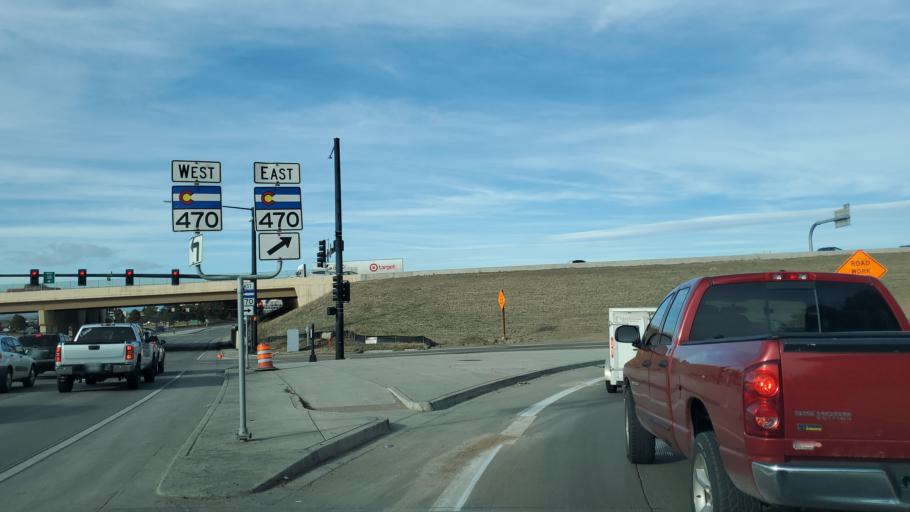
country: US
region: Colorado
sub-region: Douglas County
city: Highlands Ranch
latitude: 39.5635
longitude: -104.9870
